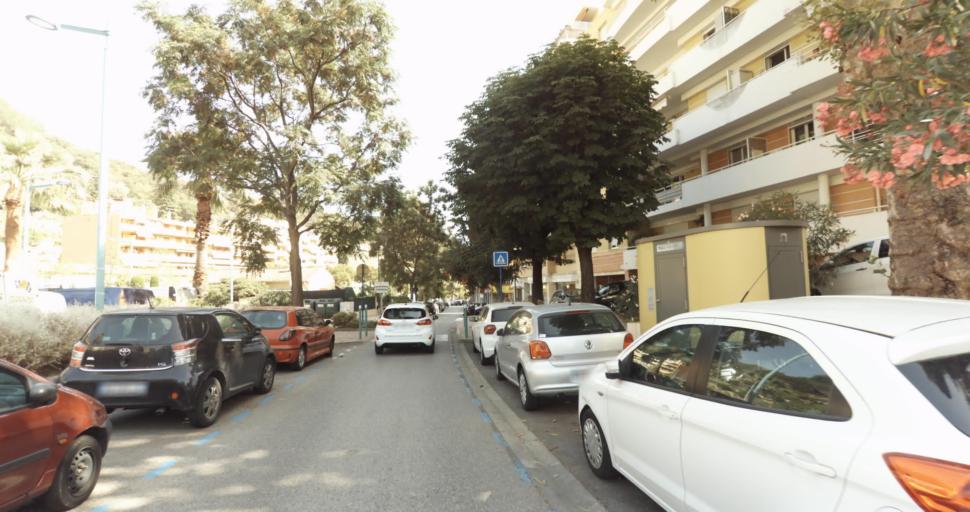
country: FR
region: Provence-Alpes-Cote d'Azur
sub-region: Departement des Alpes-Maritimes
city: Menton
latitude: 43.7858
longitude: 7.4940
